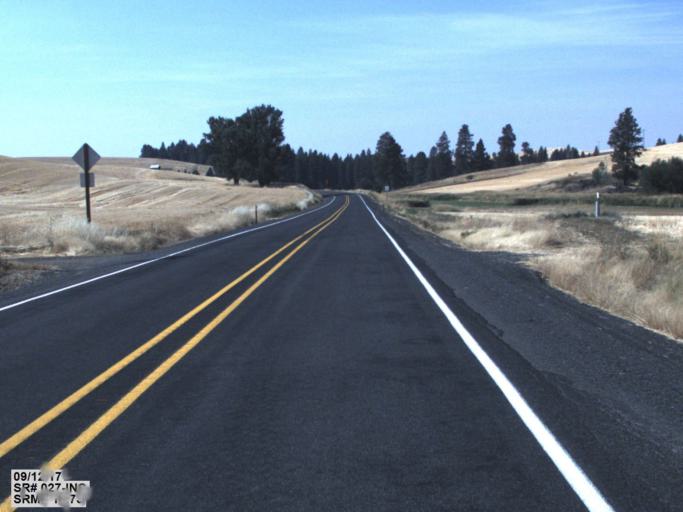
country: US
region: Washington
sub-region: Whitman County
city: Pullman
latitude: 46.9634
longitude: -117.0963
